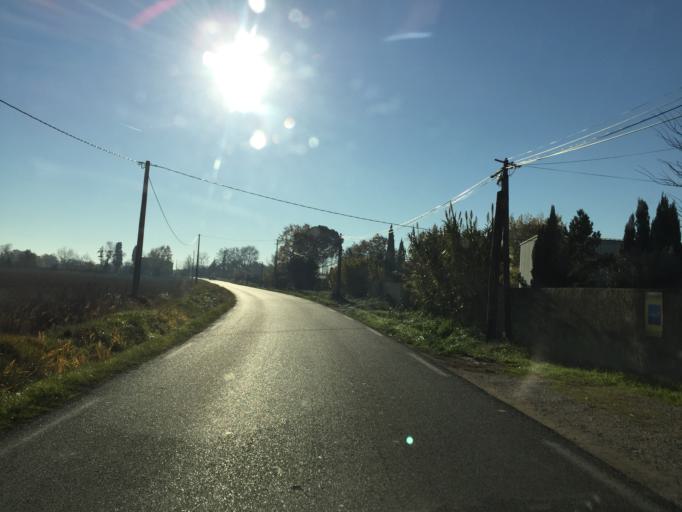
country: FR
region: Provence-Alpes-Cote d'Azur
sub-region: Departement du Vaucluse
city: Bedarrides
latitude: 44.0360
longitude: 4.9099
